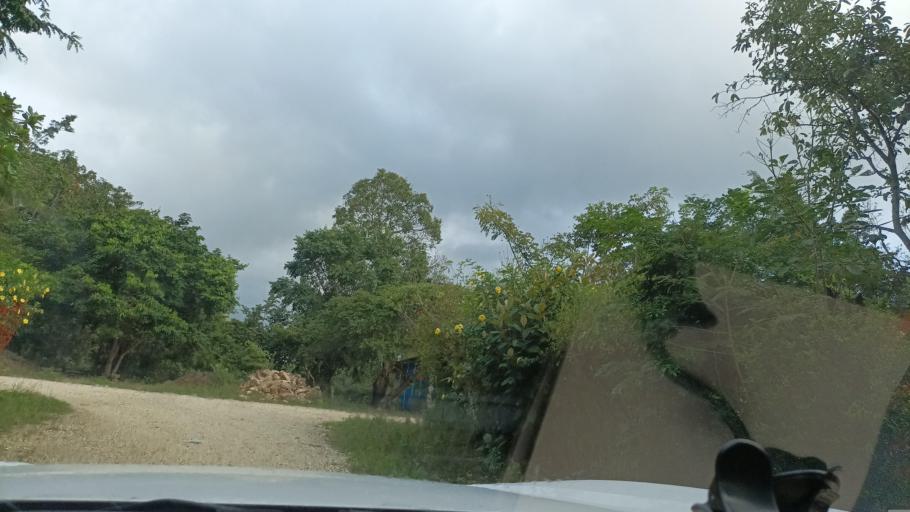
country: MX
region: Veracruz
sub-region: Moloacan
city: Cuichapa
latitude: 17.9244
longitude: -94.3672
